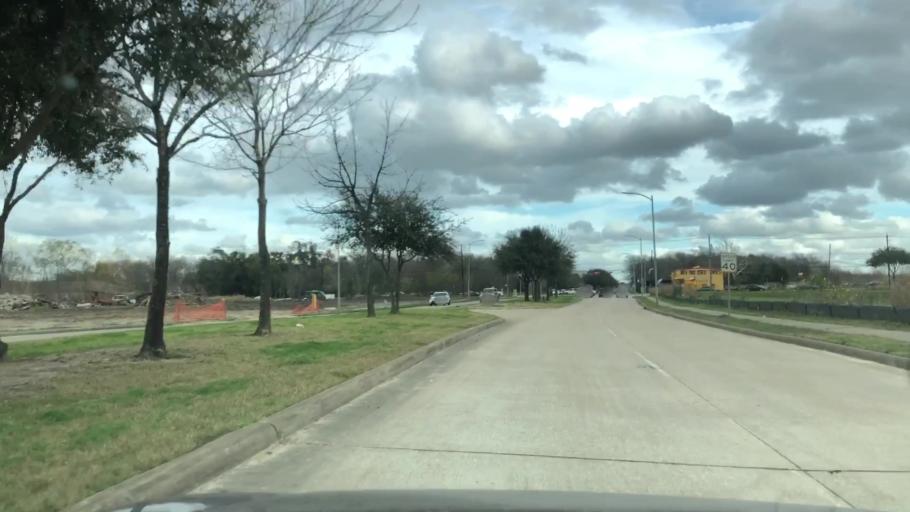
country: US
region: Texas
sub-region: Fort Bend County
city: Missouri City
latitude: 29.6121
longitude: -95.4672
